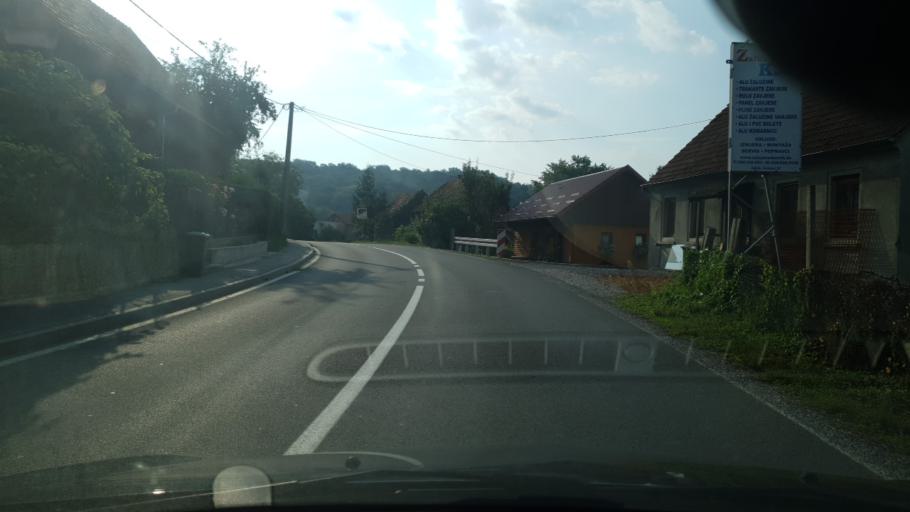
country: HR
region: Krapinsko-Zagorska
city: Zabok
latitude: 46.0224
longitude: 15.9256
